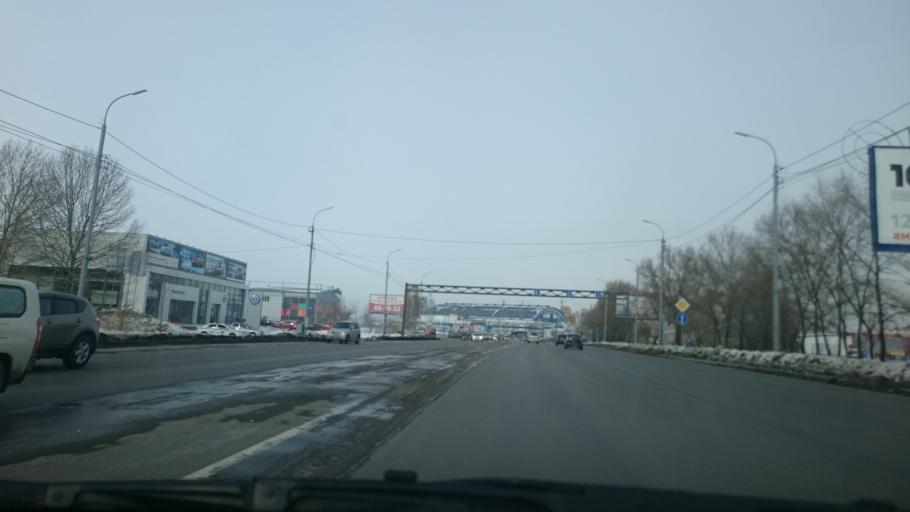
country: RU
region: Khabarovsk Krai
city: Khabarovsk Vtoroy
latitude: 48.4237
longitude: 135.1004
